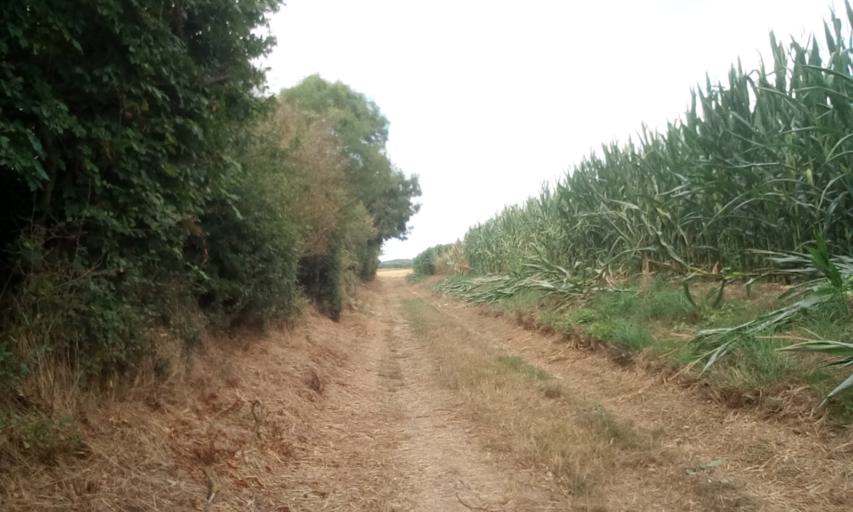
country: FR
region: Lower Normandy
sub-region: Departement du Calvados
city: Bellengreville
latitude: 49.1303
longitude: -0.1962
